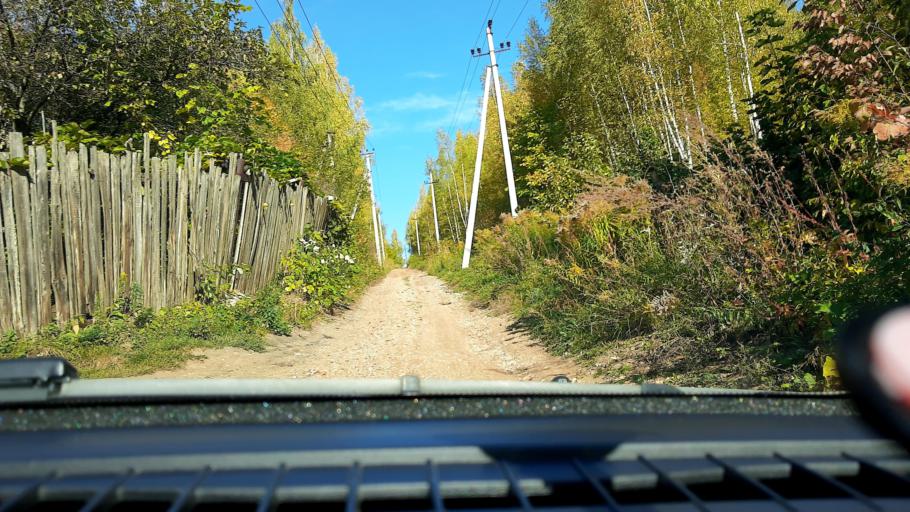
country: RU
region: Nizjnij Novgorod
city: Afonino
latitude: 56.2398
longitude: 44.0591
